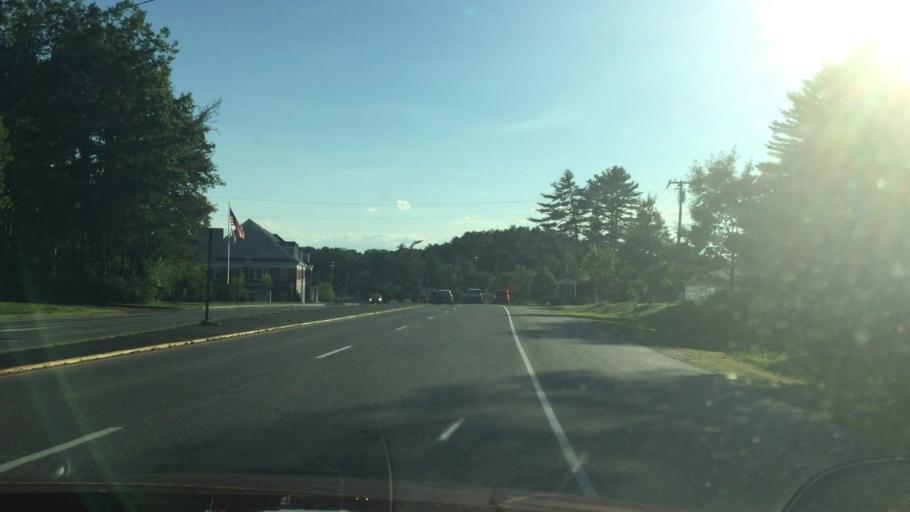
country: US
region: Maine
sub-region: Cumberland County
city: Yarmouth
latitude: 43.8039
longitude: -70.1799
